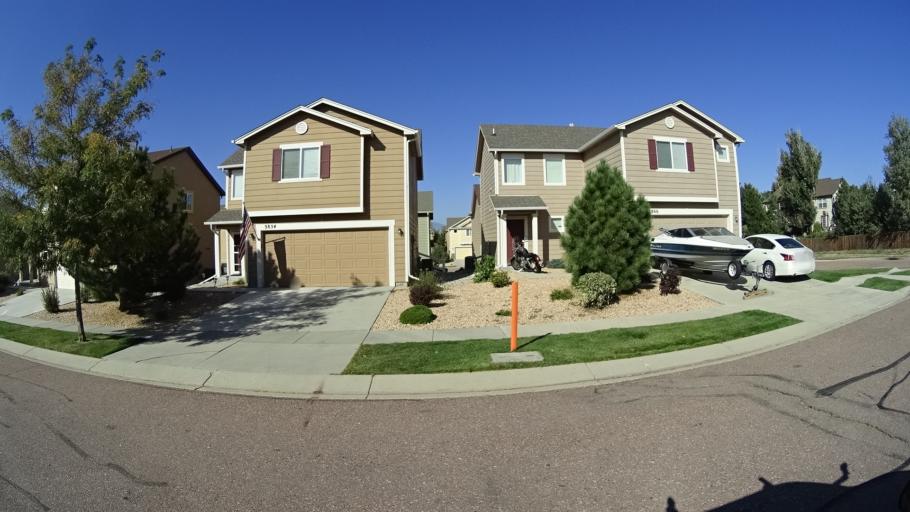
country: US
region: Colorado
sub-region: El Paso County
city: Cimarron Hills
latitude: 38.8878
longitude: -104.6977
